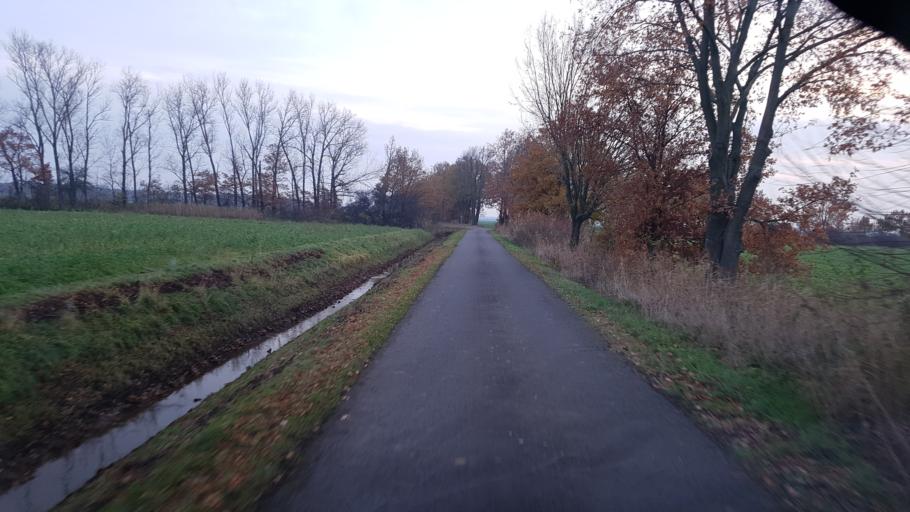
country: DE
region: Brandenburg
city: Vogelsang
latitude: 52.2256
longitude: 14.6658
